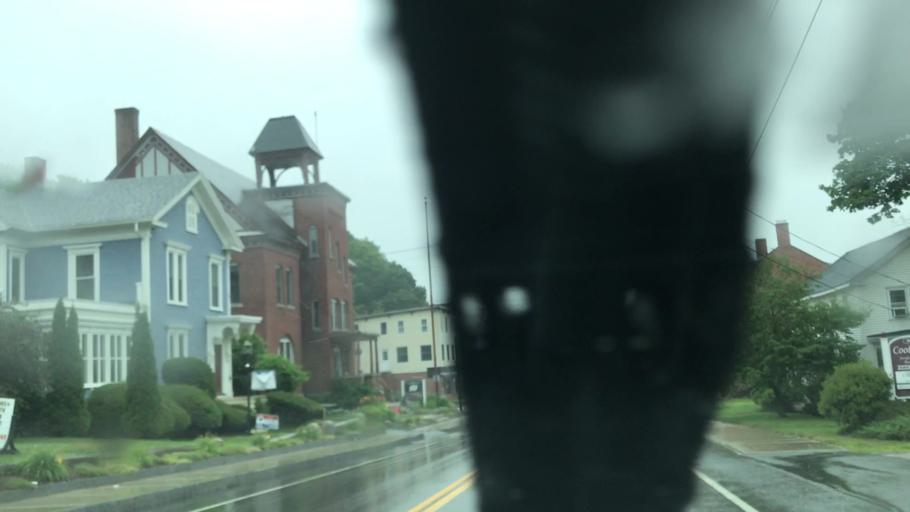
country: US
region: New Hampshire
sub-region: Strafford County
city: Somersworth
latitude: 43.2612
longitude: -70.8657
